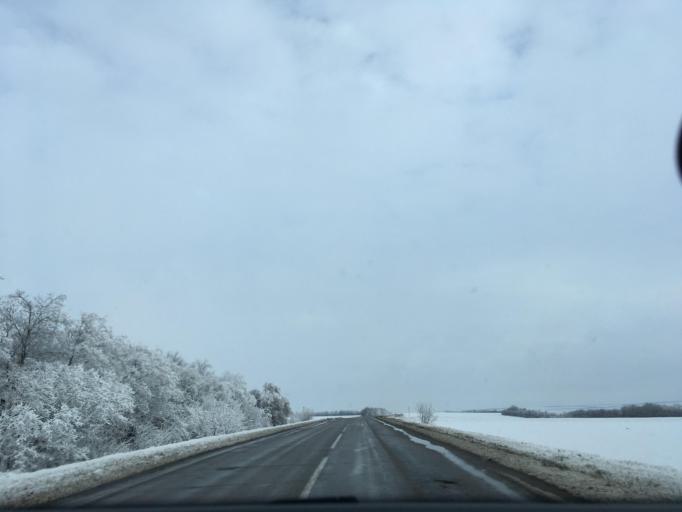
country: UA
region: Luhansk
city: Lozno-Oleksandrivka
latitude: 49.9921
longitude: 39.0245
